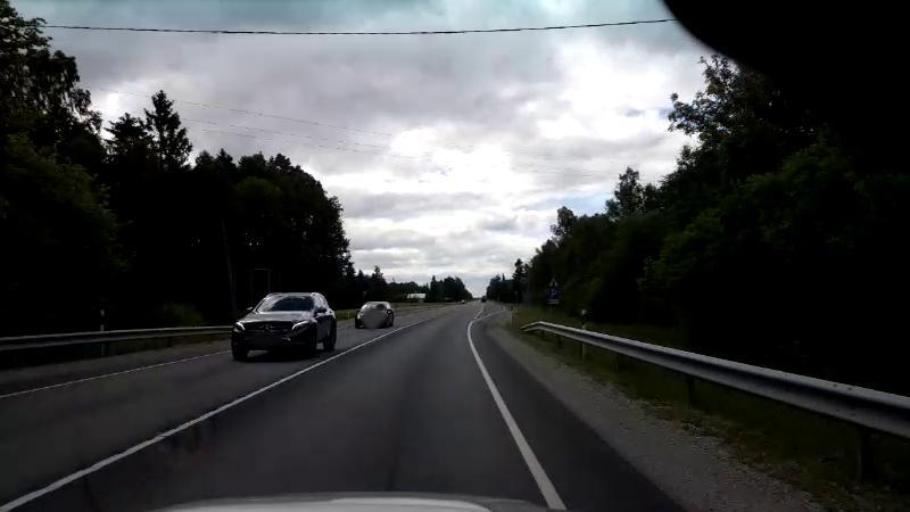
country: EE
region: Paernumaa
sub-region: Halinga vald
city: Parnu-Jaagupi
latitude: 58.6557
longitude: 24.4748
